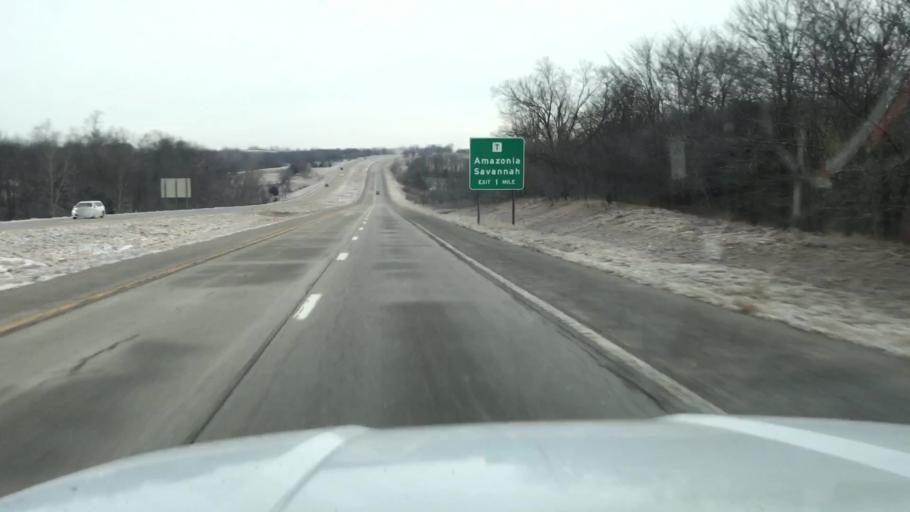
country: US
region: Missouri
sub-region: Andrew County
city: Savannah
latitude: 39.9037
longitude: -94.8577
